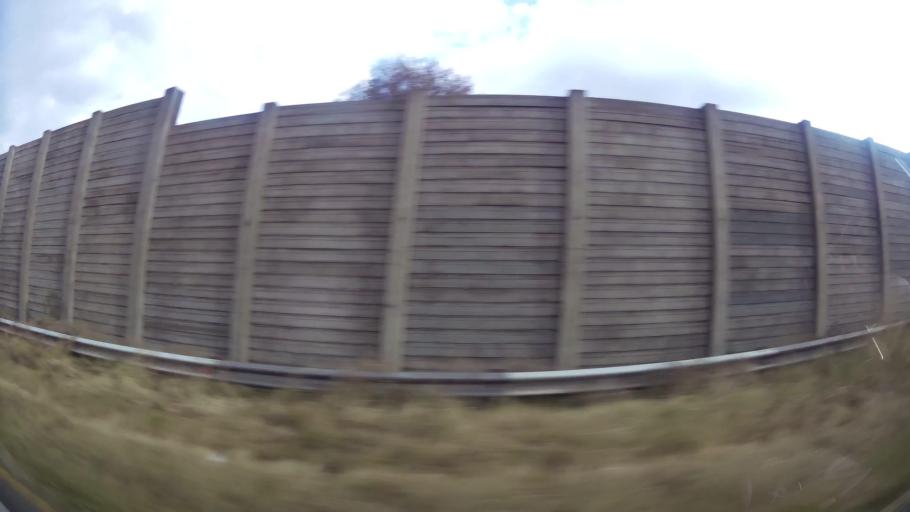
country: ZA
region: Orange Free State
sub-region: Fezile Dabi District Municipality
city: Sasolburg
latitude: -26.8296
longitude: 27.8545
